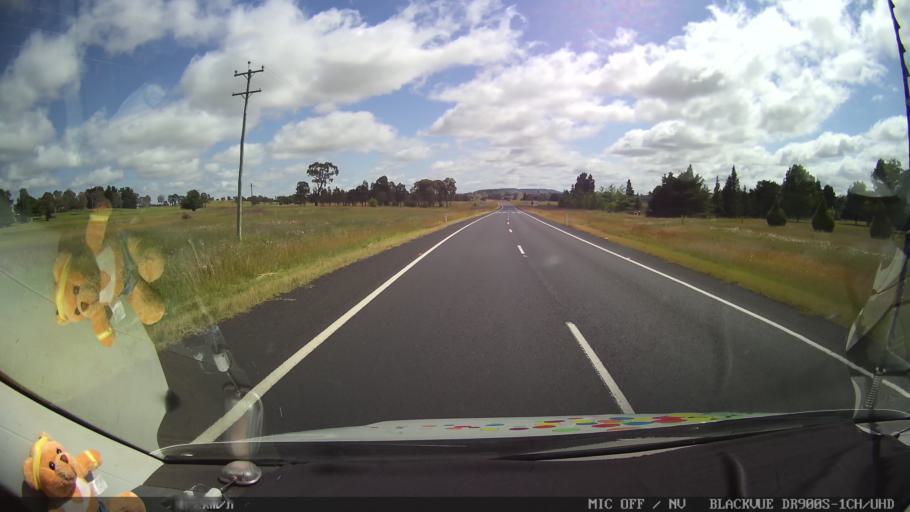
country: AU
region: New South Wales
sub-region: Glen Innes Severn
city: Glen Innes
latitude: -29.9202
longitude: 151.7256
